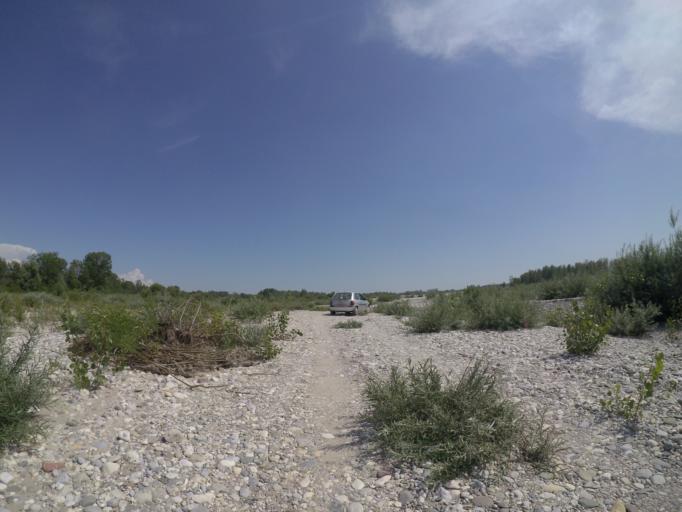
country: IT
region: Friuli Venezia Giulia
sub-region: Provincia di Udine
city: Camino al Tagliamento
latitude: 45.9098
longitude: 12.9216
